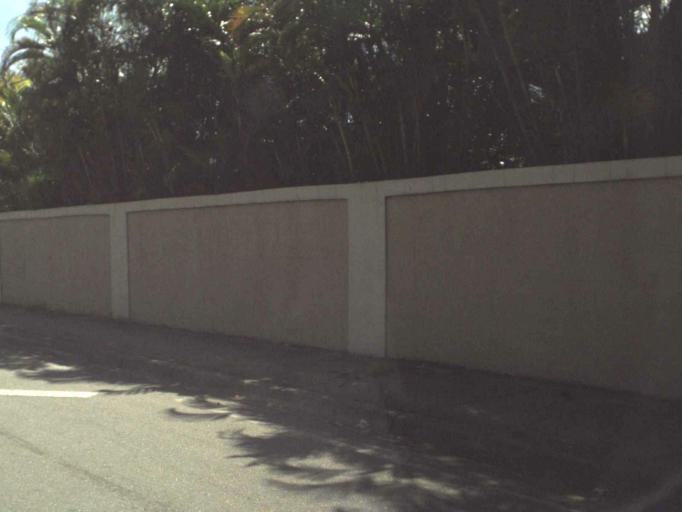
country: US
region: Florida
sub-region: Miami-Dade County
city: Glenvar Heights
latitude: 25.7023
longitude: -80.3332
